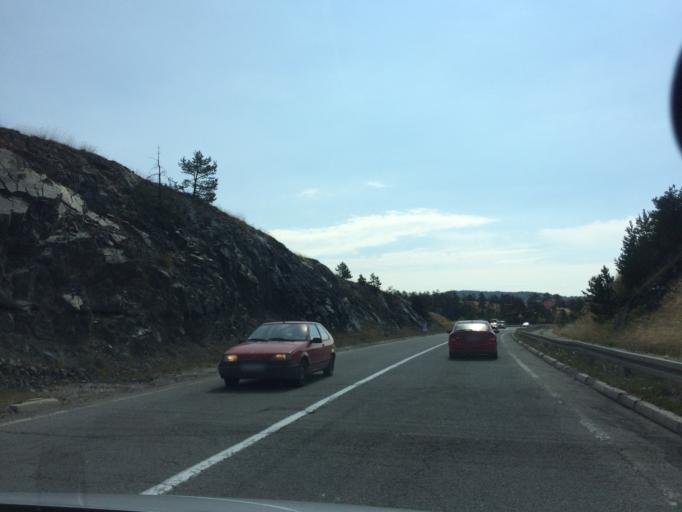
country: RS
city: Zlatibor
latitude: 43.6353
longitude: 19.7224
